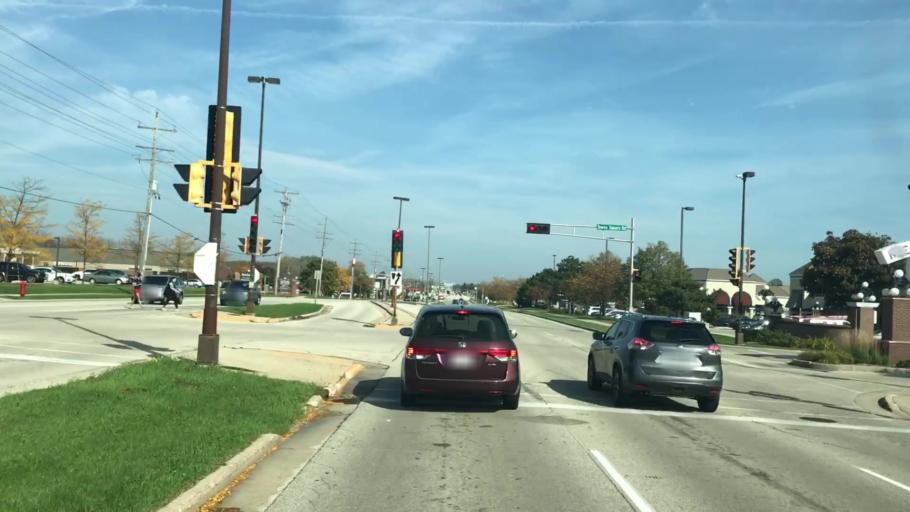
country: US
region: Wisconsin
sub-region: Milwaukee County
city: River Hills
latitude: 43.2179
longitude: -87.9240
